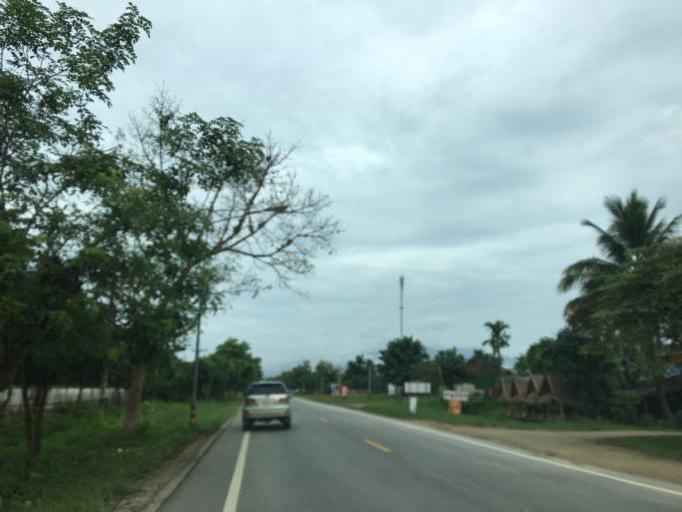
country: TH
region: Chiang Rai
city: Mae Lao
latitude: 19.8421
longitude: 99.7217
